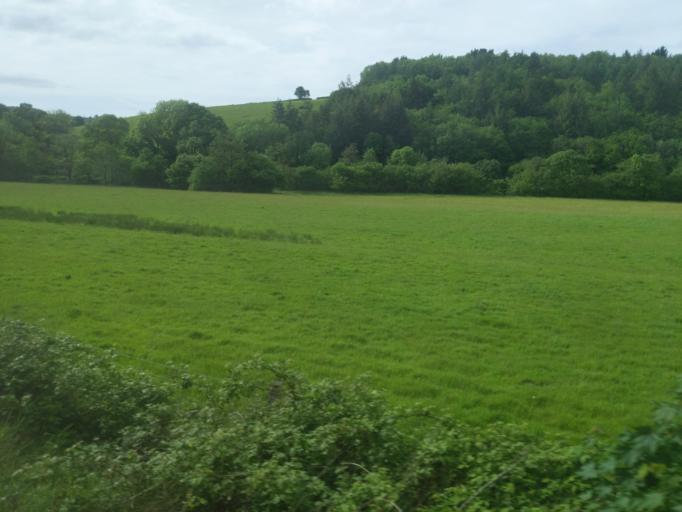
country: GB
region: England
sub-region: Devon
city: Winkleigh
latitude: 50.9566
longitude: -3.9539
